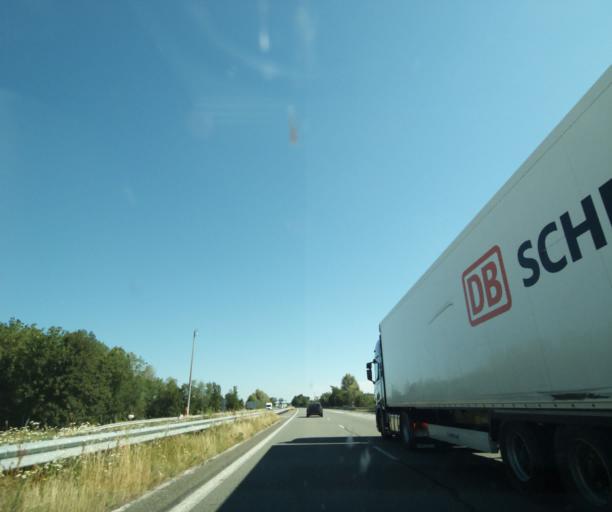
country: FR
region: Champagne-Ardenne
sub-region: Departement de la Haute-Marne
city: Avrecourt
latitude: 47.9935
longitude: 5.5128
